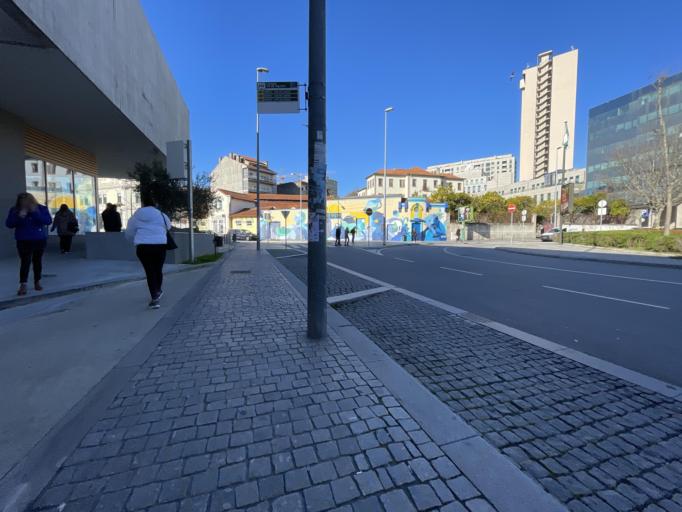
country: PT
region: Porto
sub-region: Porto
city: Porto
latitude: 41.1492
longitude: -8.5993
